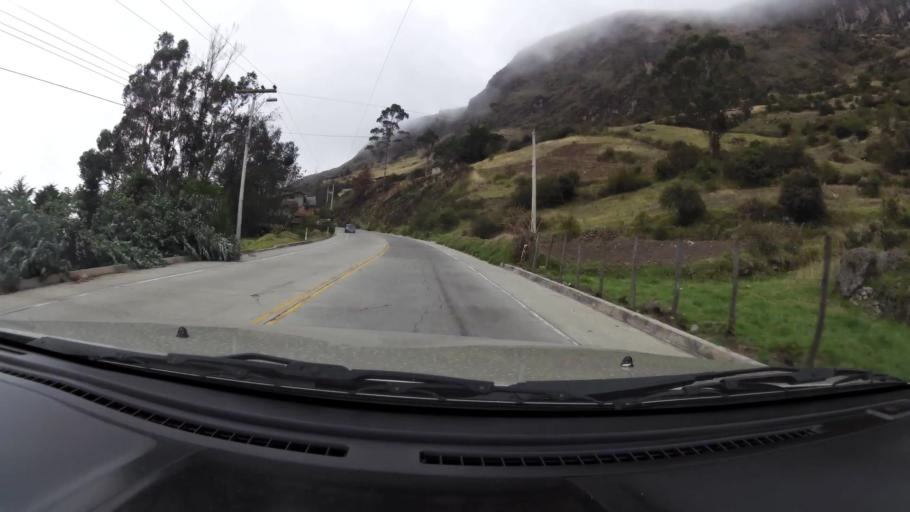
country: EC
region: Canar
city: Canar
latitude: -2.4833
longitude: -78.9918
